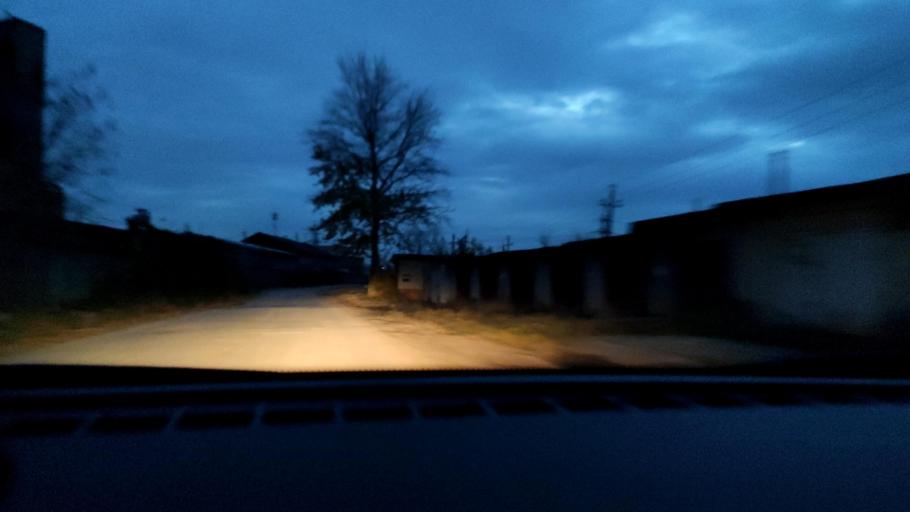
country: RU
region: Perm
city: Froly
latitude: 57.9515
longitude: 56.2411
